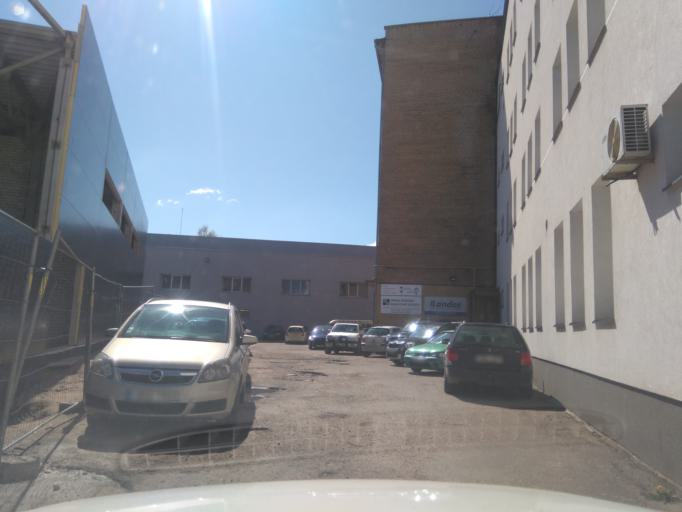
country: LT
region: Kauno apskritis
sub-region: Kaunas
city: Aleksotas
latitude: 54.8743
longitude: 23.9364
